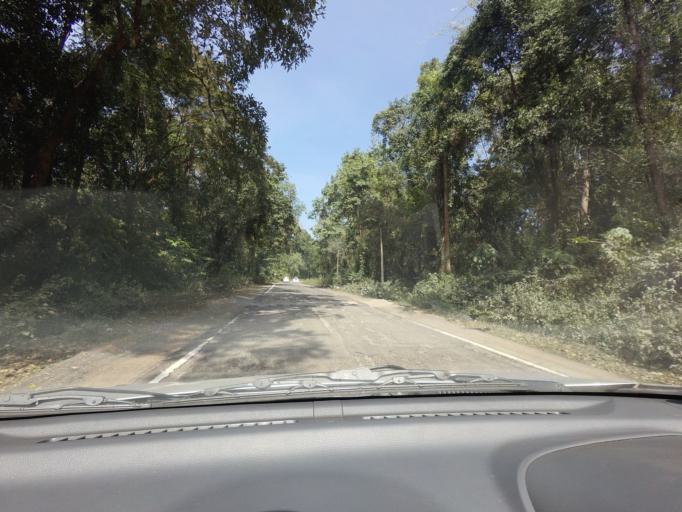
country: IN
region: Karnataka
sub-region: Dakshina Kannada
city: Sulya
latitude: 12.7314
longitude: 75.5960
